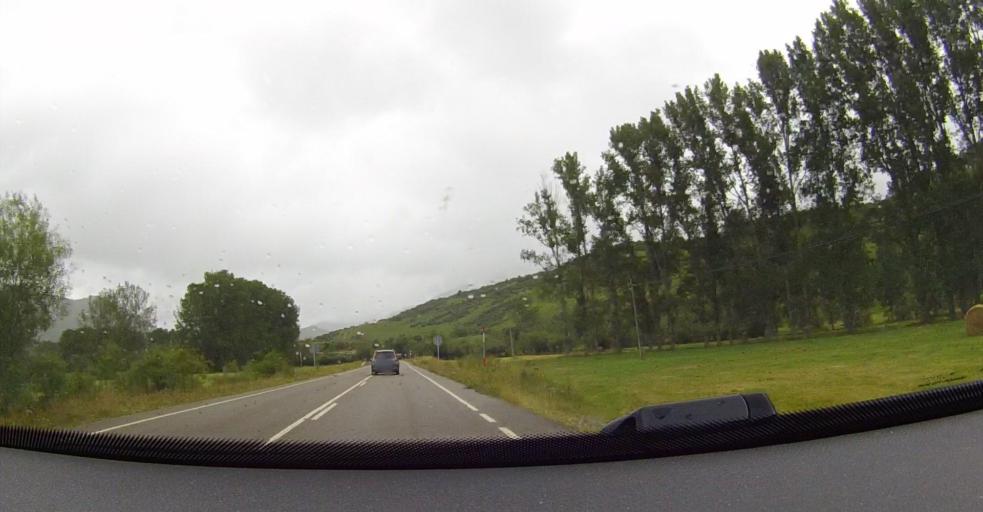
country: ES
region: Castille and Leon
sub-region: Provincia de Leon
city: Acebedo
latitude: 43.0466
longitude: -5.1267
